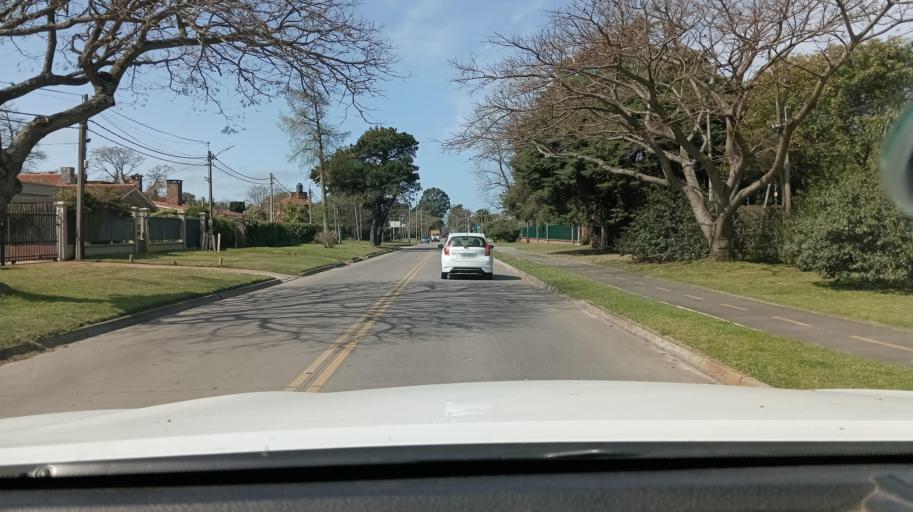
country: UY
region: Canelones
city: Paso de Carrasco
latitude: -34.8756
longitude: -56.0542
